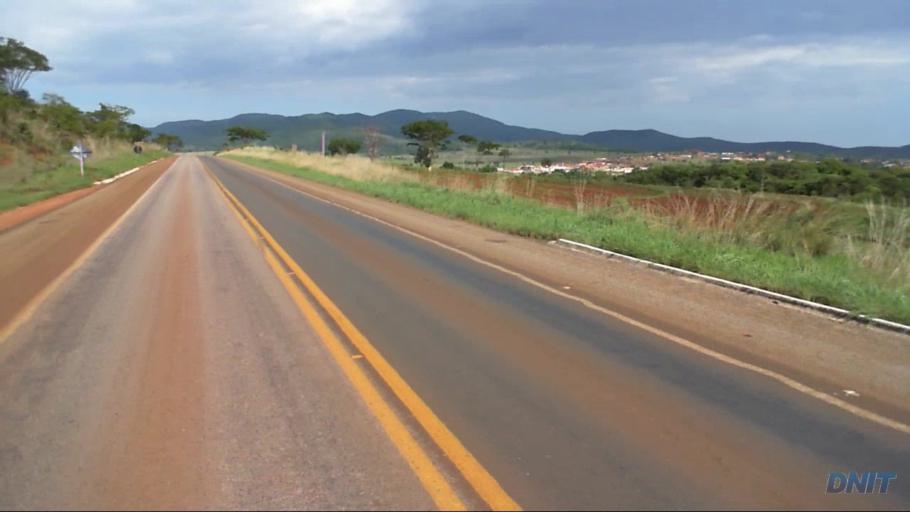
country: BR
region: Goias
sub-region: Barro Alto
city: Barro Alto
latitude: -14.9879
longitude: -48.9124
